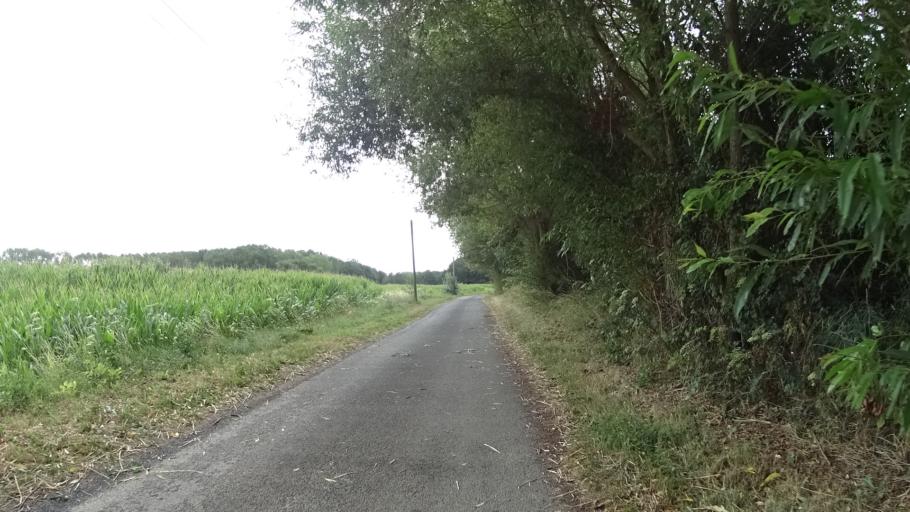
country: FR
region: Pays de la Loire
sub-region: Departement de Maine-et-Loire
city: Montjean-sur-Loire
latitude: 47.3831
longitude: -0.8335
